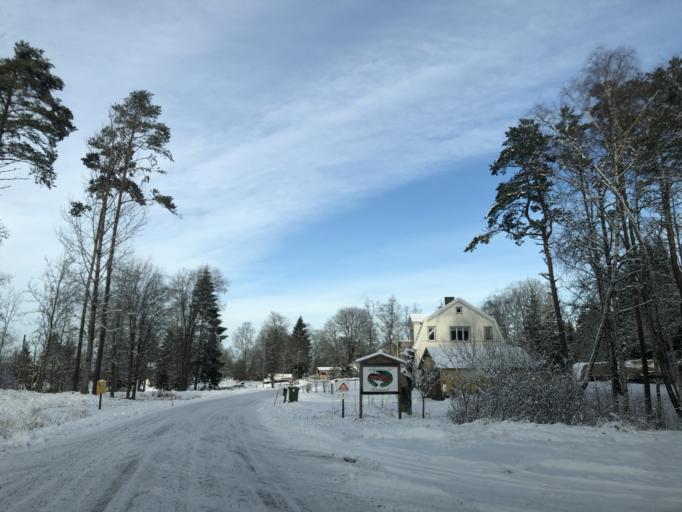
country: SE
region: Vaestra Goetaland
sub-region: Ulricehamns Kommun
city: Ulricehamn
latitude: 57.7775
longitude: 13.5229
